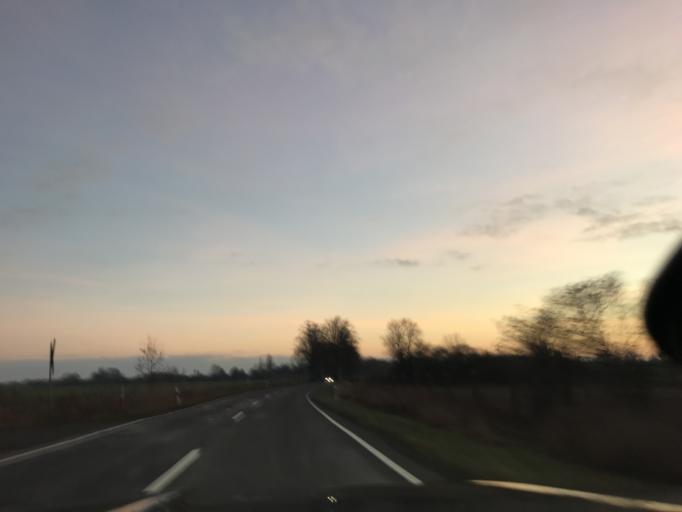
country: DE
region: Brandenburg
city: Ketzin
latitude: 52.4943
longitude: 12.8508
